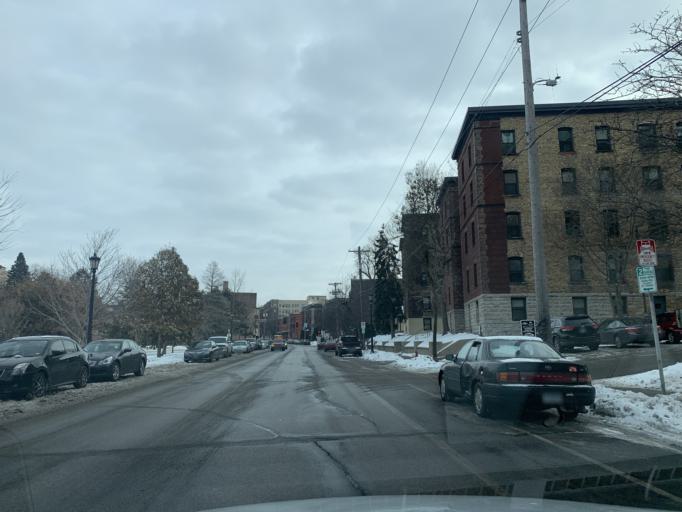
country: US
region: Minnesota
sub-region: Hennepin County
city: Minneapolis
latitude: 44.9680
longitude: -93.2837
